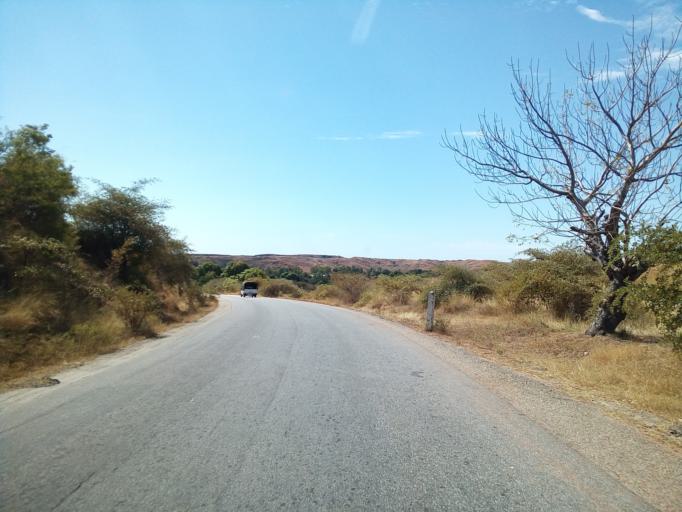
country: MG
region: Betsiboka
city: Maevatanana
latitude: -16.9179
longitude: 46.8689
